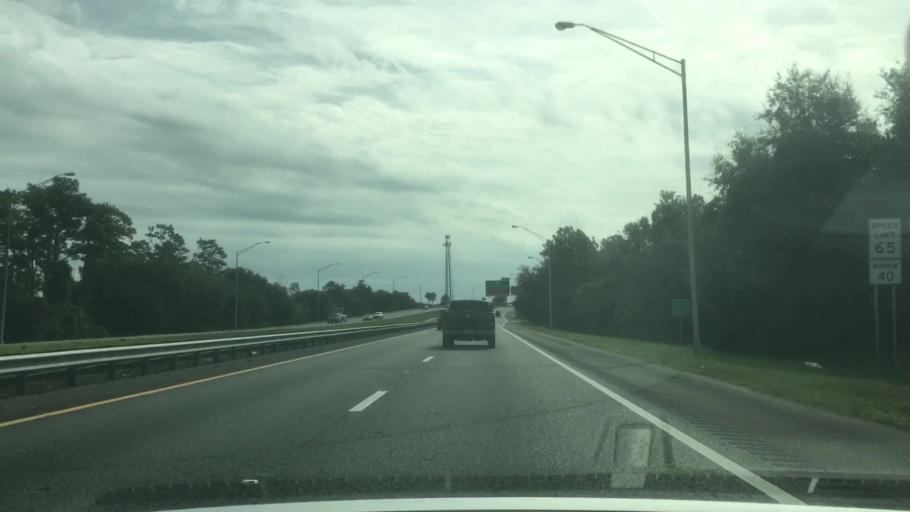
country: US
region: Florida
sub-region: Duval County
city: Jacksonville
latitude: 30.4245
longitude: -81.5707
